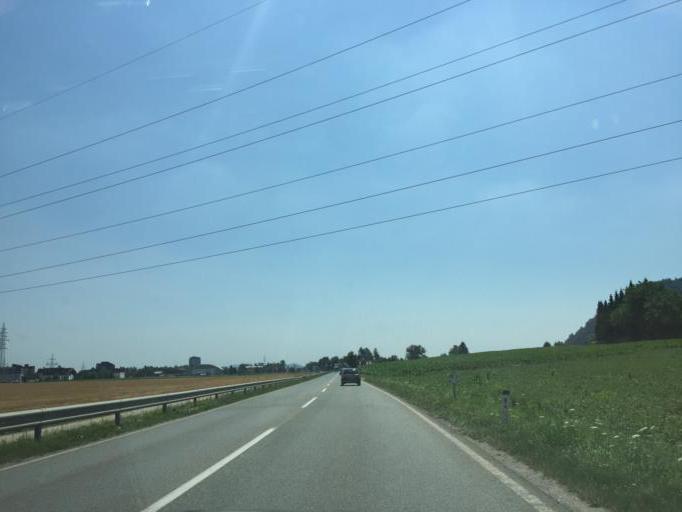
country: SI
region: Kranj
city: Kranj
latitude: 46.2556
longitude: 14.3406
